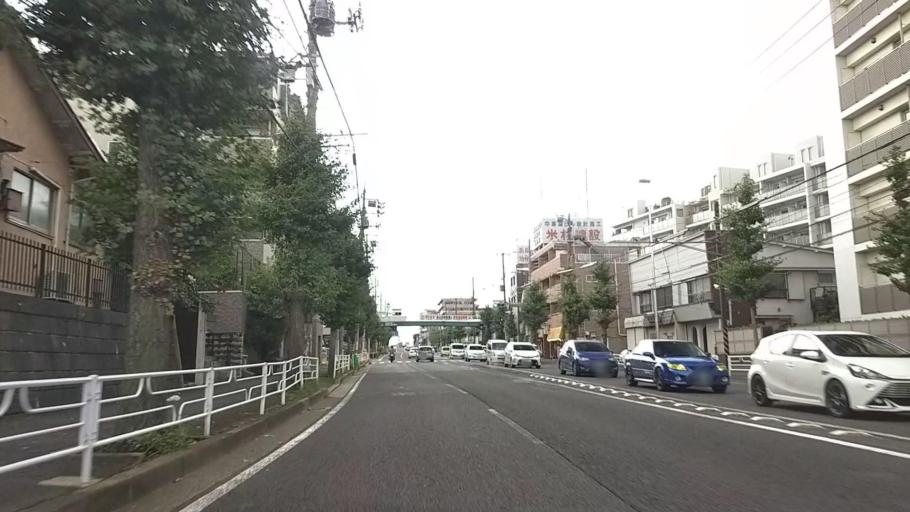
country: JP
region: Kanagawa
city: Yokohama
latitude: 35.4834
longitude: 139.6021
